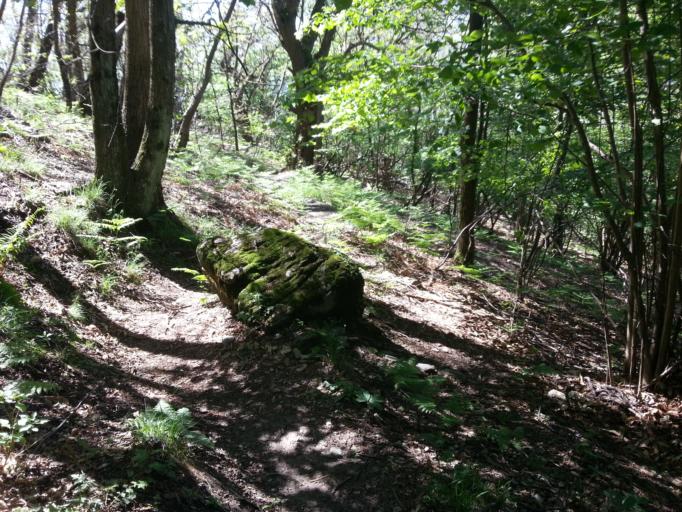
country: IT
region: Lombardy
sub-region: Provincia di Como
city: Codogna-Cardano
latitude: 46.0418
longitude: 9.2144
